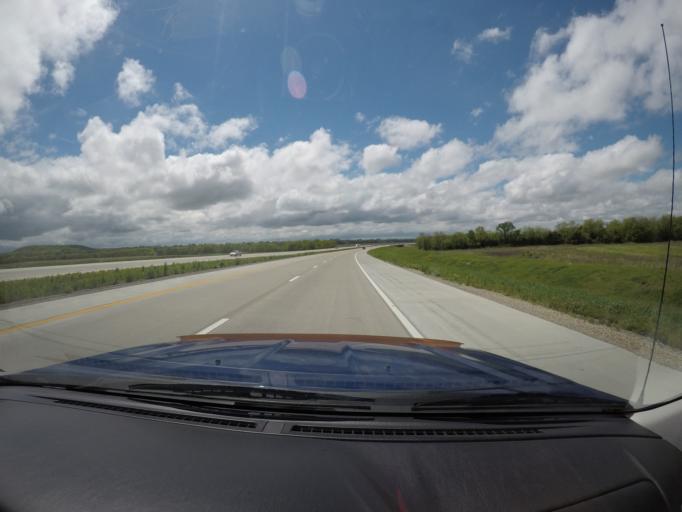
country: US
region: Kansas
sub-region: Douglas County
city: Lawrence
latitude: 38.9261
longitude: -95.1837
